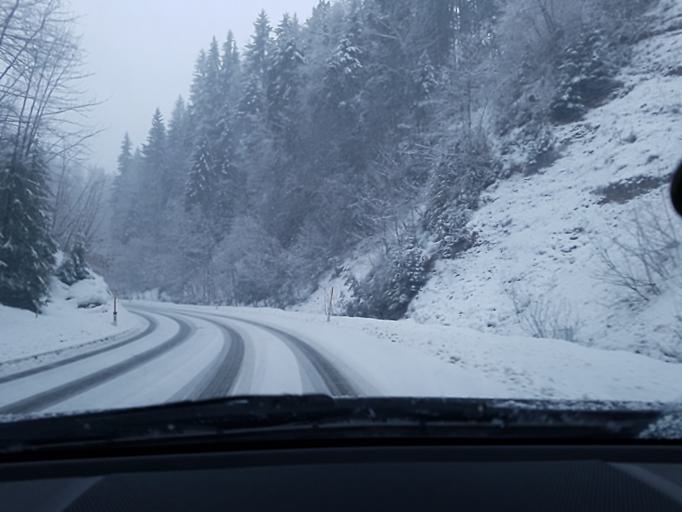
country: AT
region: Salzburg
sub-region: Politischer Bezirk Hallein
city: Abtenau
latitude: 47.5728
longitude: 13.3797
